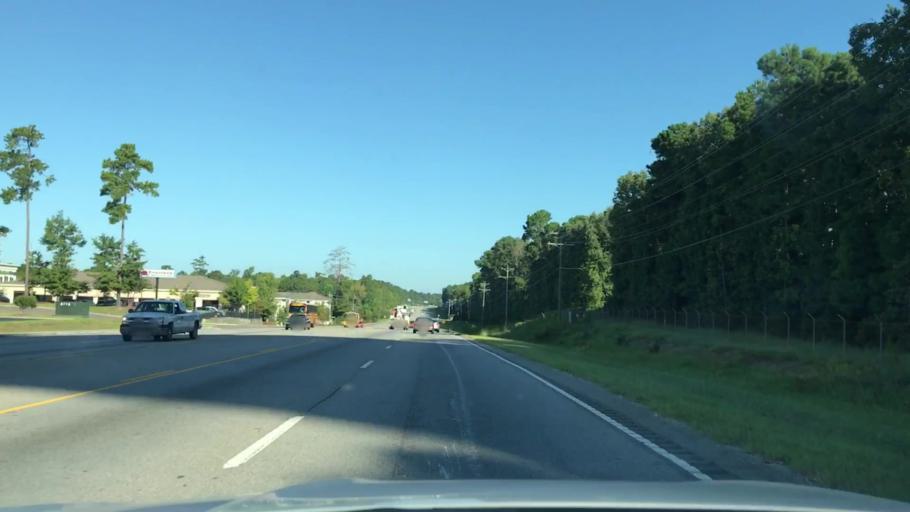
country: US
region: South Carolina
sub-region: Berkeley County
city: Goose Creek
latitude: 33.0363
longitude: -80.0635
